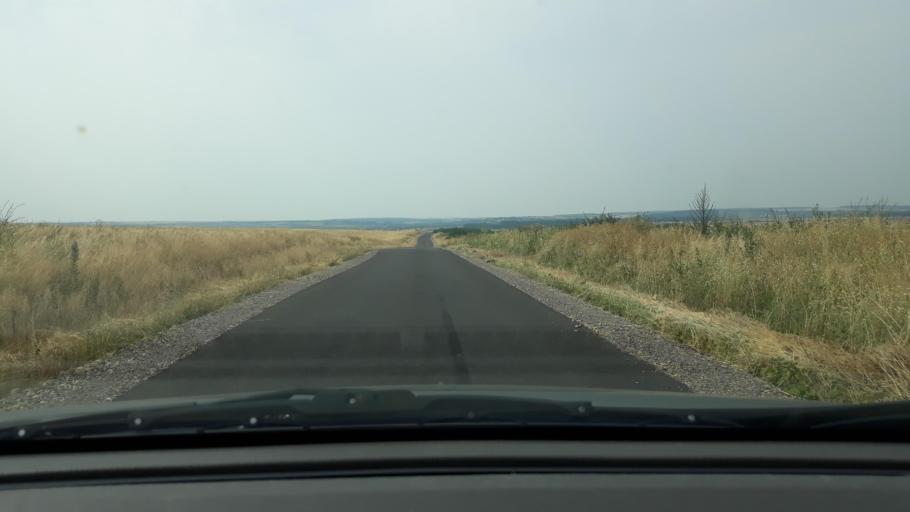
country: RO
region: Bihor
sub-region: Comuna Chislaz
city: Misca
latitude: 47.2728
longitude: 22.2835
